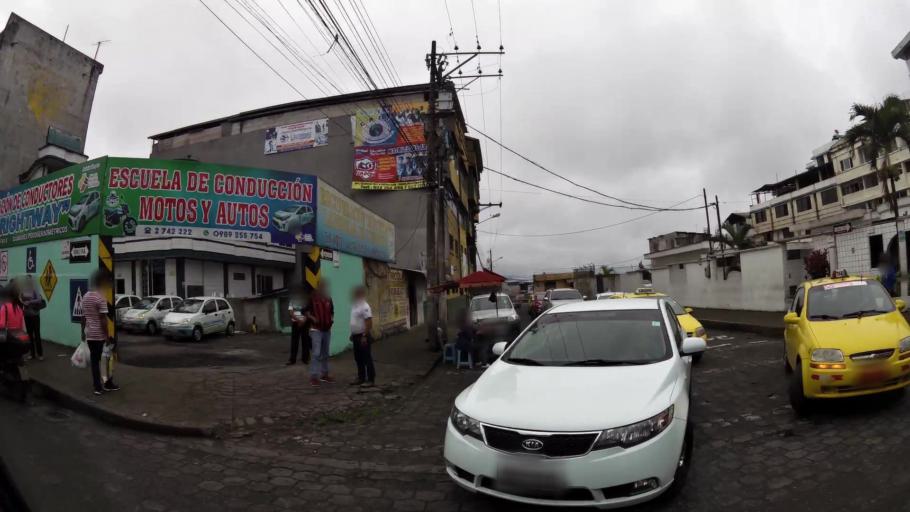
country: EC
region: Santo Domingo de los Tsachilas
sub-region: Canton Santo Domingo de los Colorados
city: Santo Domingo de los Colorados
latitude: -0.2557
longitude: -79.1736
